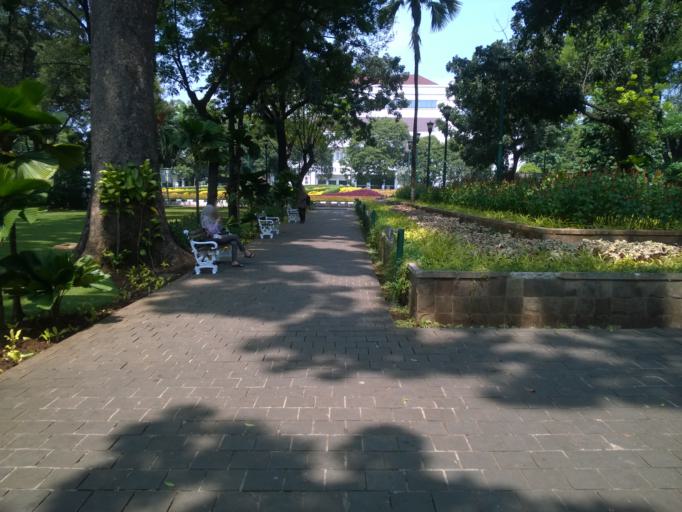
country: ID
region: Jakarta Raya
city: Jakarta
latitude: -6.1995
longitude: 106.8326
